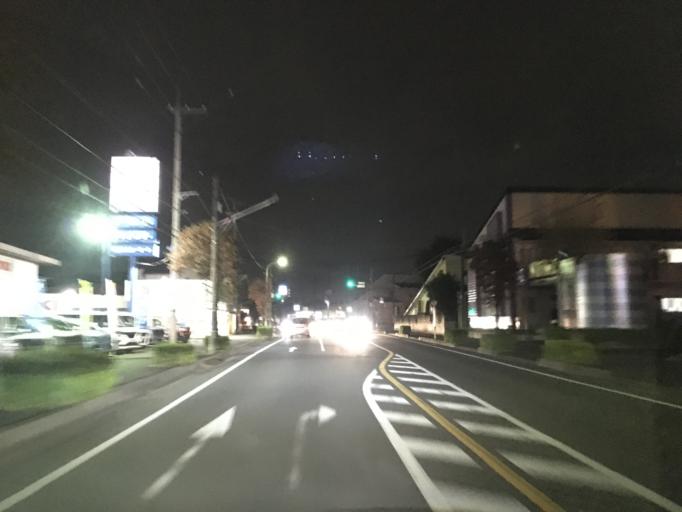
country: JP
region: Saitama
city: Sayama
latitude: 35.8646
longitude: 139.3989
